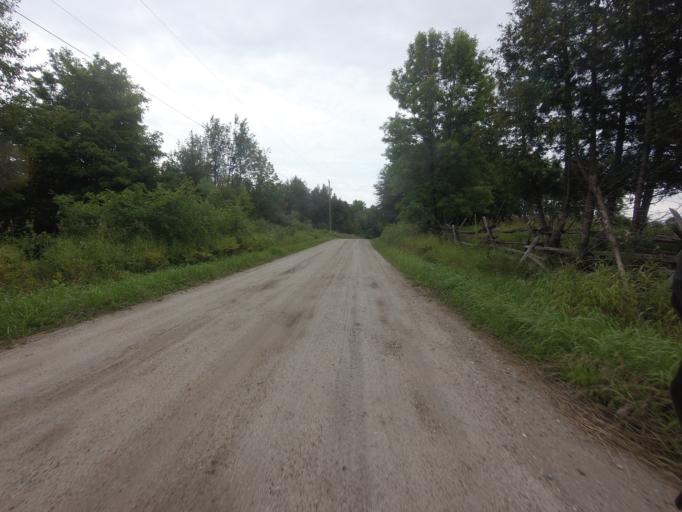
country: CA
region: Ontario
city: Perth
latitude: 45.0527
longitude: -76.3937
